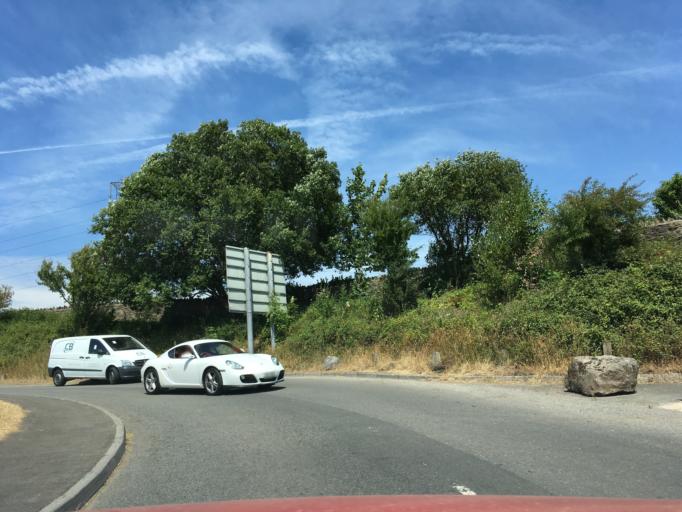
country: GB
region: Wales
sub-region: Caerphilly County Borough
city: Machen
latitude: 51.5426
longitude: -3.1287
